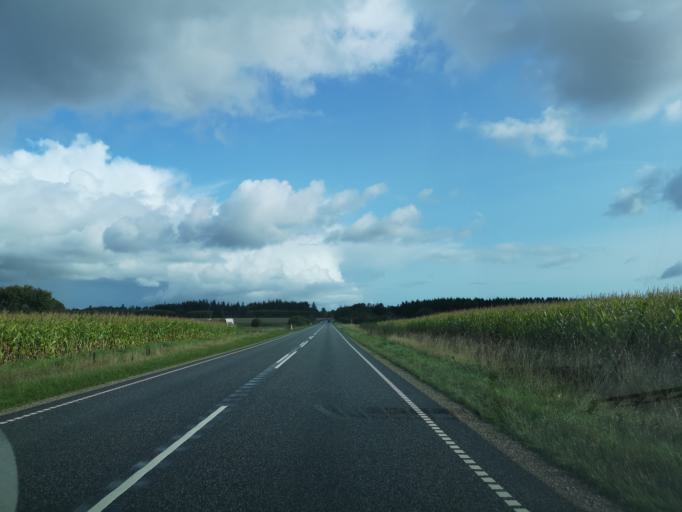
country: DK
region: Central Jutland
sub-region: Ringkobing-Skjern Kommune
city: Videbaek
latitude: 56.0341
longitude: 8.6092
